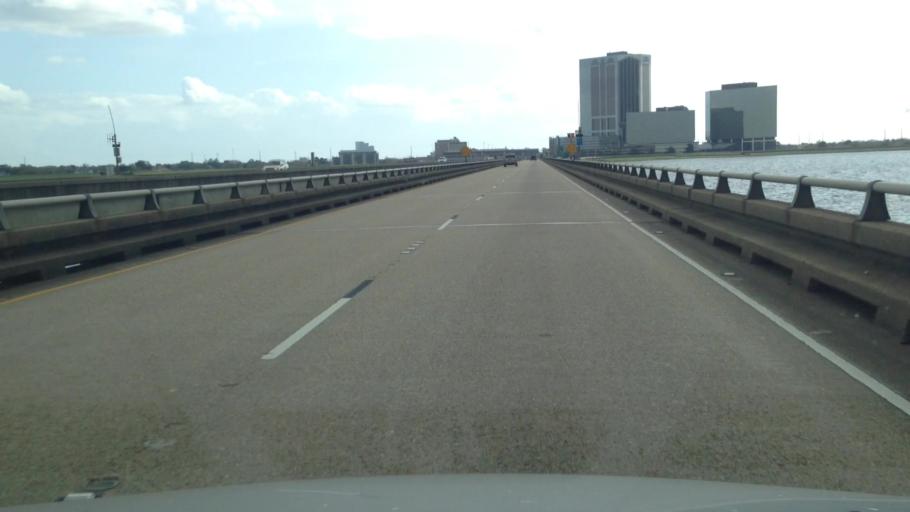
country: US
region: Louisiana
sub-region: Jefferson Parish
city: Metairie
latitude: 30.0286
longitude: -90.1529
